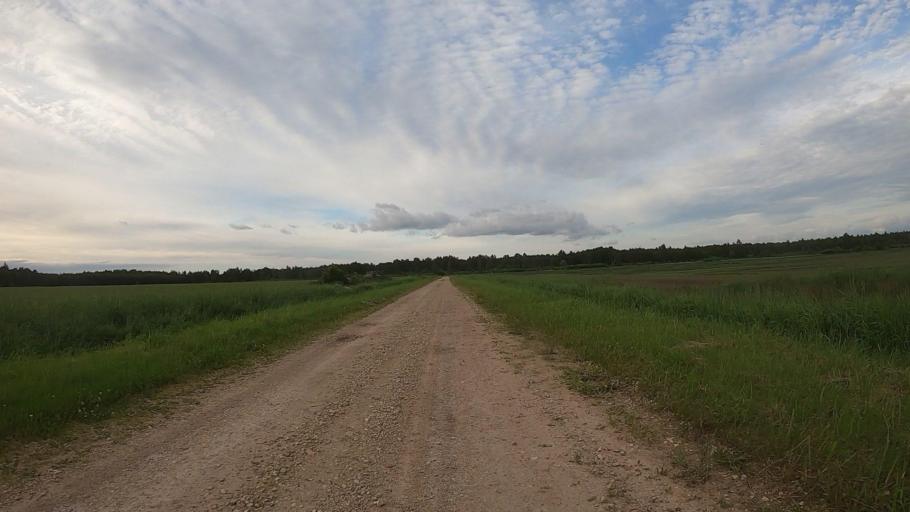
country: LV
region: Olaine
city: Olaine
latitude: 56.8259
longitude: 23.9581
